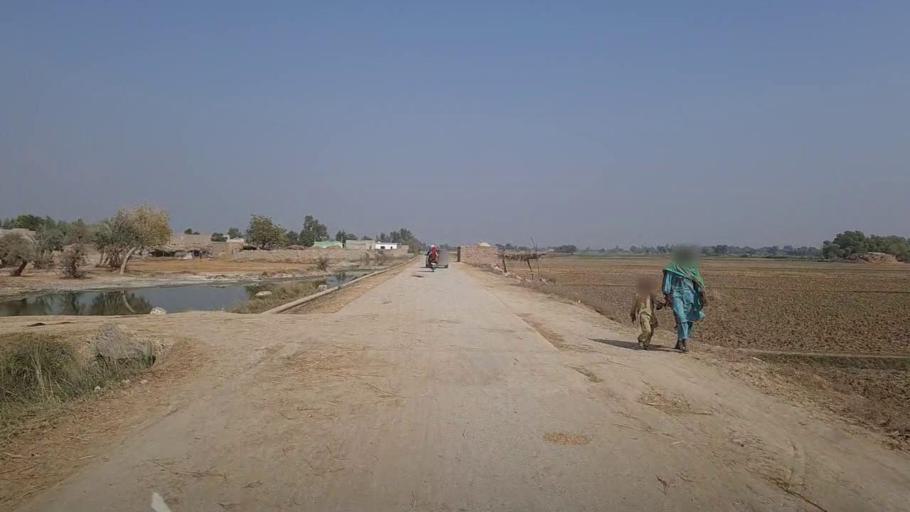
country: PK
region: Sindh
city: Kandhkot
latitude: 28.2313
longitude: 69.2147
